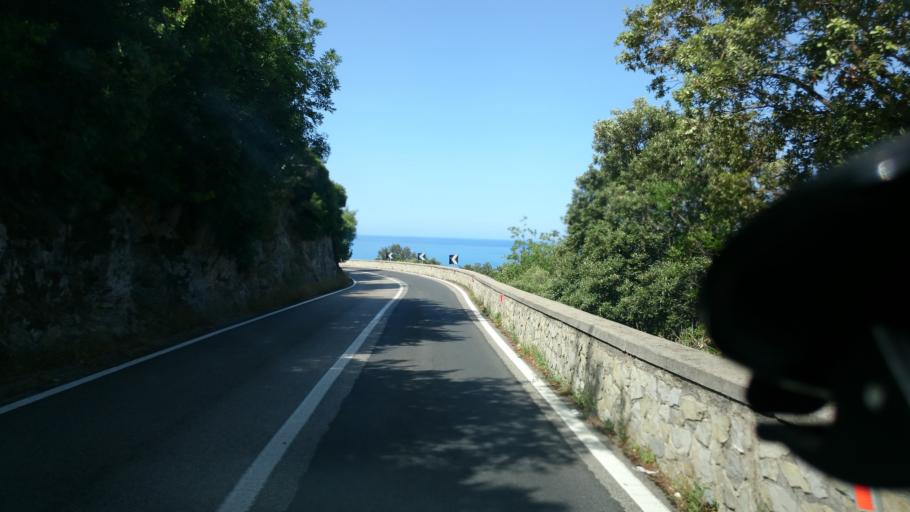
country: IT
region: Basilicate
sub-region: Provincia di Potenza
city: Maratea
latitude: 39.9928
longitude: 15.7134
